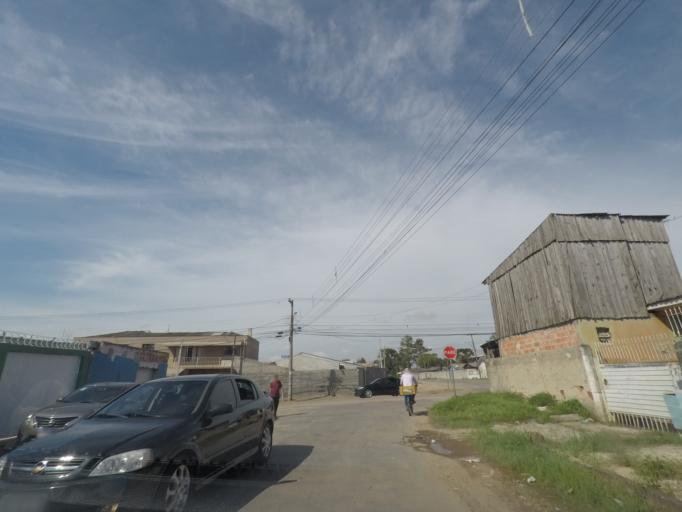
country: BR
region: Parana
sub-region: Curitiba
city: Curitiba
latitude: -25.4677
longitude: -49.2622
